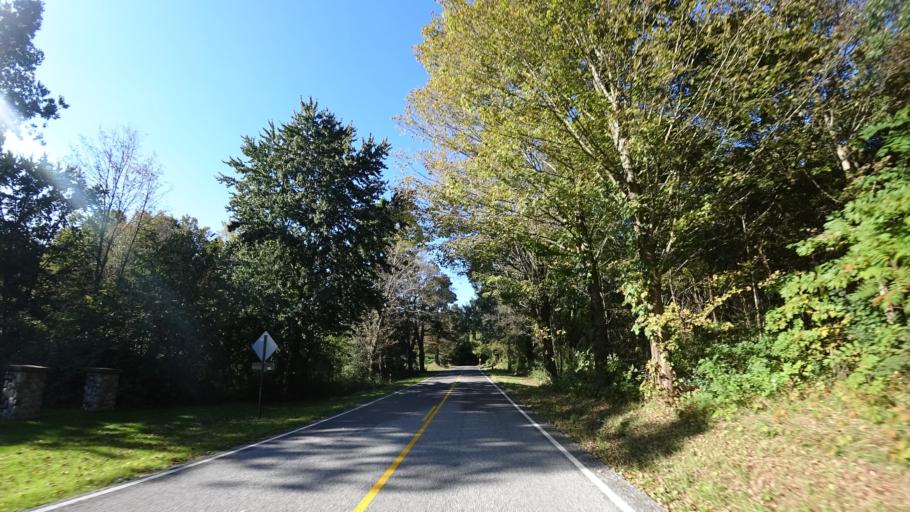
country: US
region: Michigan
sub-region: Berrien County
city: Benton Heights
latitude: 42.1550
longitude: -86.4193
